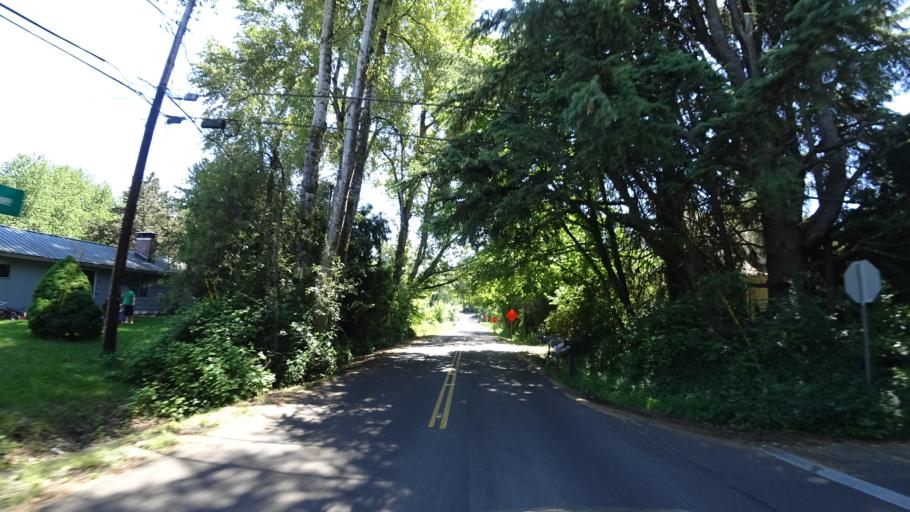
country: US
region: Oregon
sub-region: Washington County
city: Rockcreek
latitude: 45.5247
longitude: -122.9093
